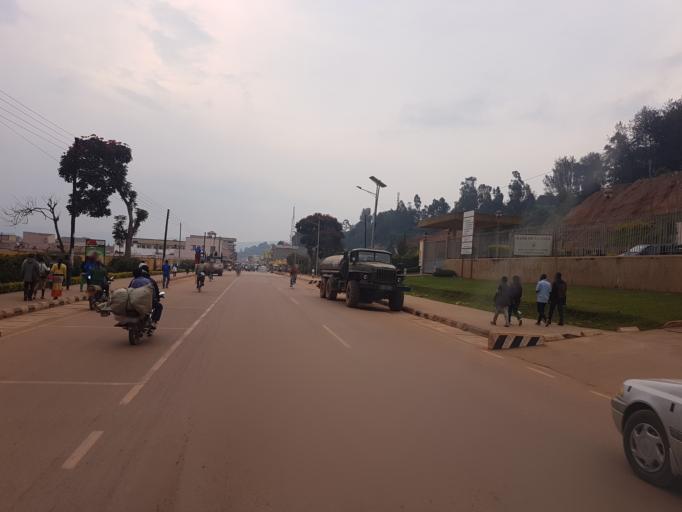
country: UG
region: Western Region
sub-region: Kabale District
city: Kabale
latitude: -1.2555
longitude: 29.9891
